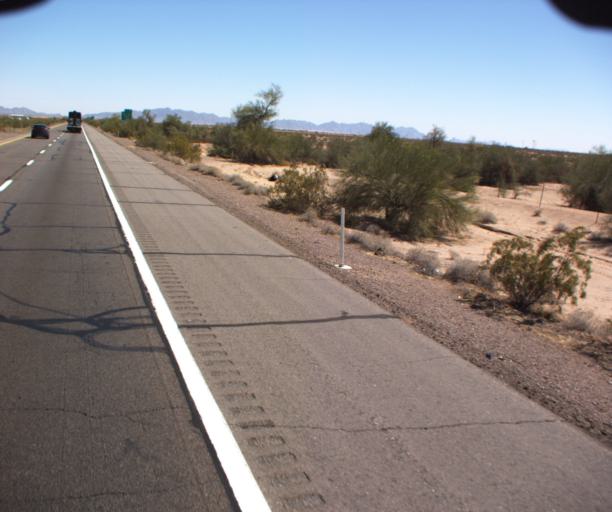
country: US
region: Arizona
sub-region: Yuma County
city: Wellton
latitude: 32.6898
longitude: -113.9769
